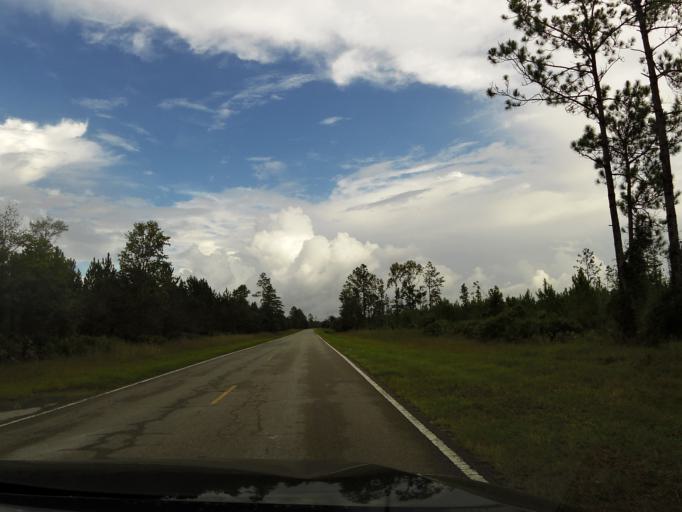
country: US
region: Florida
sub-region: Duval County
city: Baldwin
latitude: 30.4001
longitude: -81.9650
